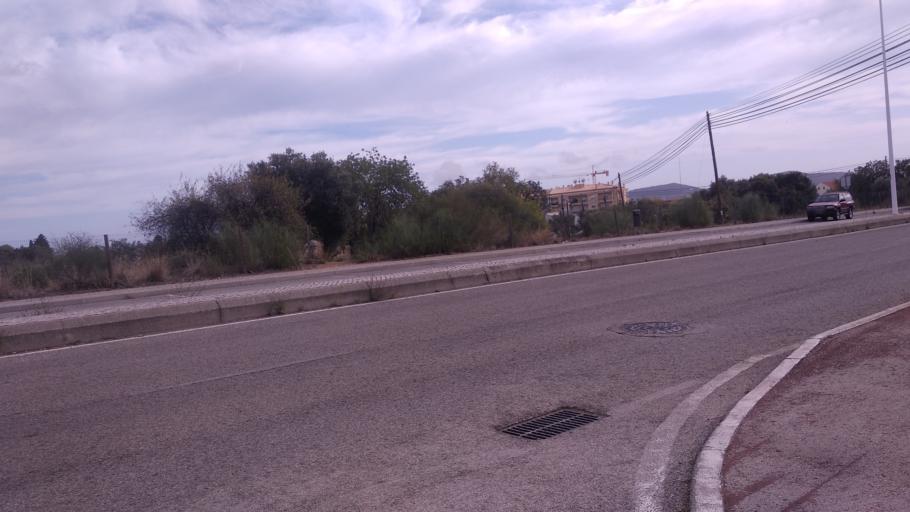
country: PT
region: Faro
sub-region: Sao Bras de Alportel
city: Sao Bras de Alportel
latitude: 37.1552
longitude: -7.8974
